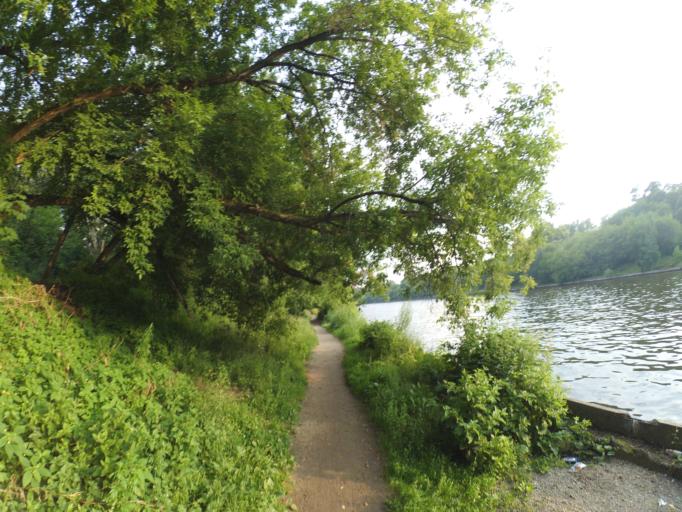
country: RU
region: Moscow
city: Shchukino
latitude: 55.7853
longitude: 37.4465
